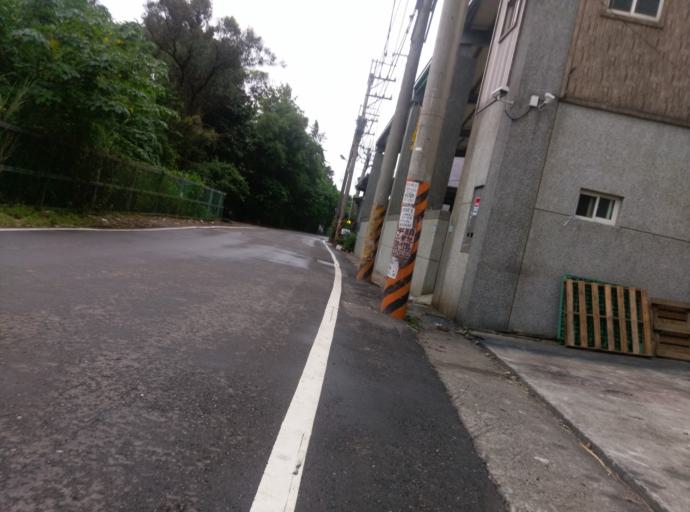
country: TW
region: Taiwan
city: Daxi
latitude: 24.9102
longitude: 121.2403
